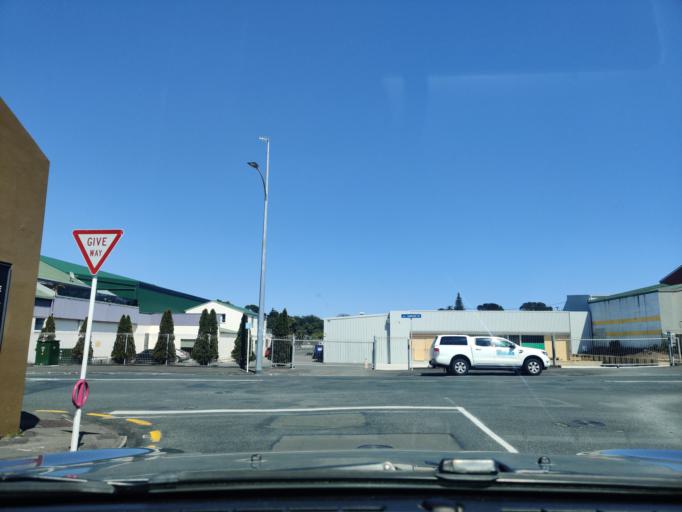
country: NZ
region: Taranaki
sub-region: New Plymouth District
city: New Plymouth
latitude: -39.0588
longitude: 174.0682
